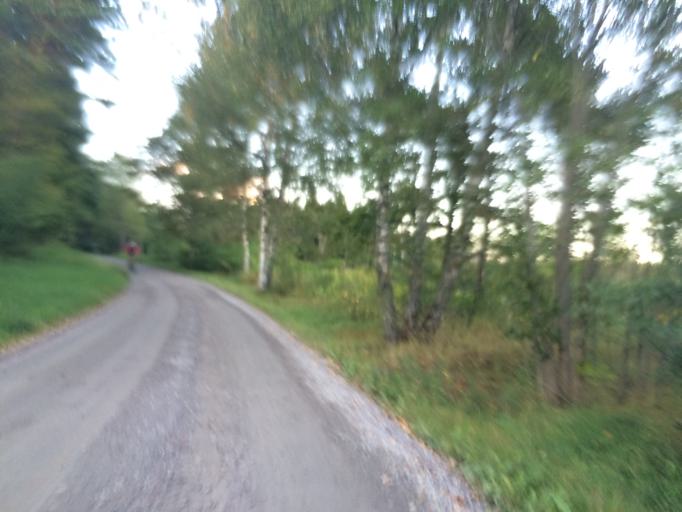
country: SE
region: Soedermanland
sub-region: Eskilstuna Kommun
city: Kvicksund
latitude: 59.4468
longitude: 16.3545
